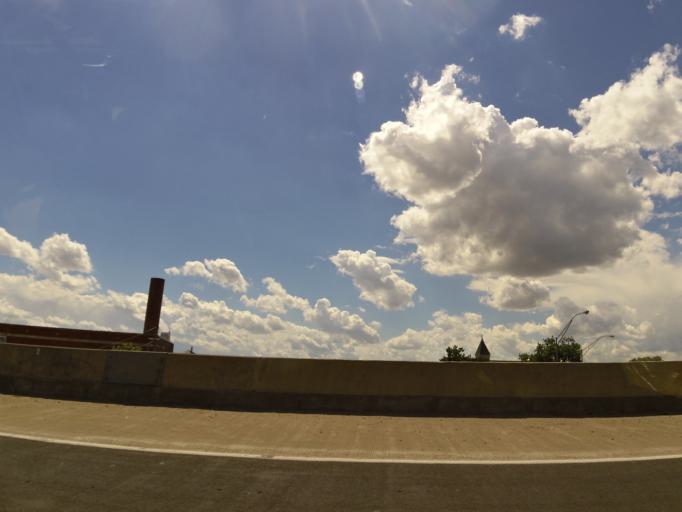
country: US
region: Iowa
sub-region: Linn County
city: Cedar Rapids
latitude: 41.9750
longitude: -91.6766
